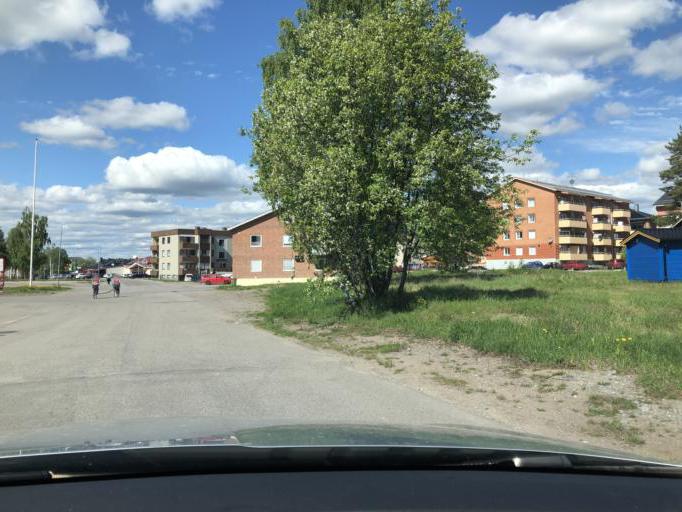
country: SE
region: Norrbotten
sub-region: Alvsbyns Kommun
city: AElvsbyn
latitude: 65.6708
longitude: 21.0121
